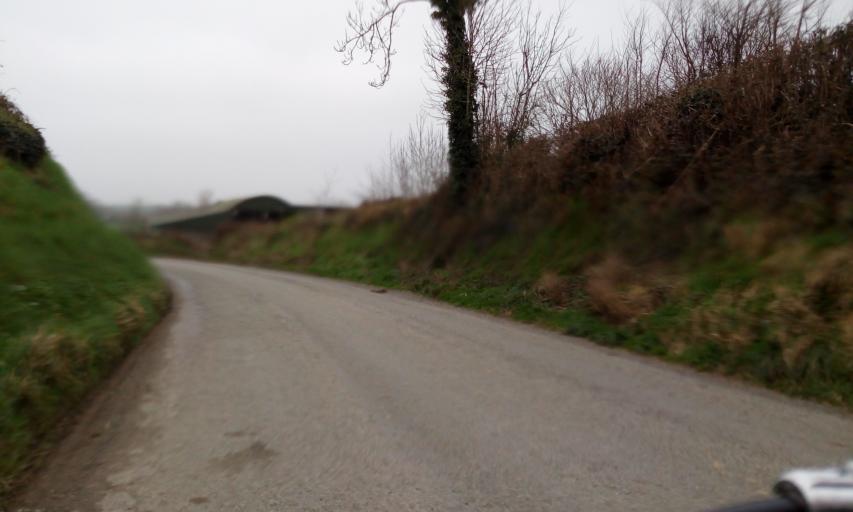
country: IE
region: Leinster
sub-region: Kilkenny
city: Kilkenny
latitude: 52.6583
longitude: -7.1778
